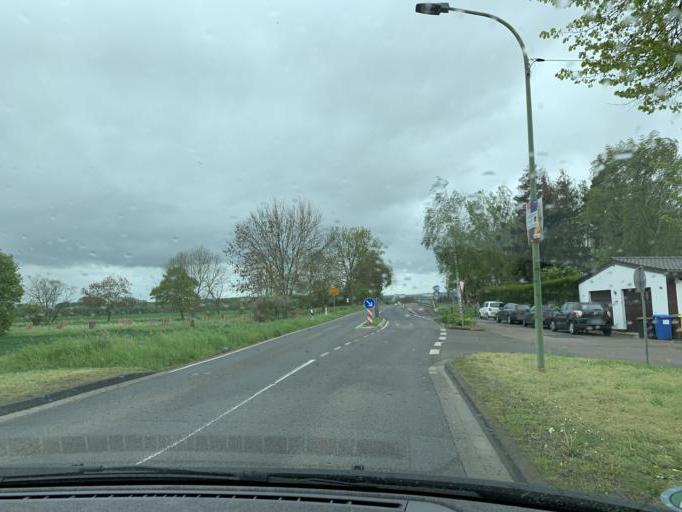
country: DE
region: North Rhine-Westphalia
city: Zulpich
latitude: 50.6712
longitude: 6.6492
